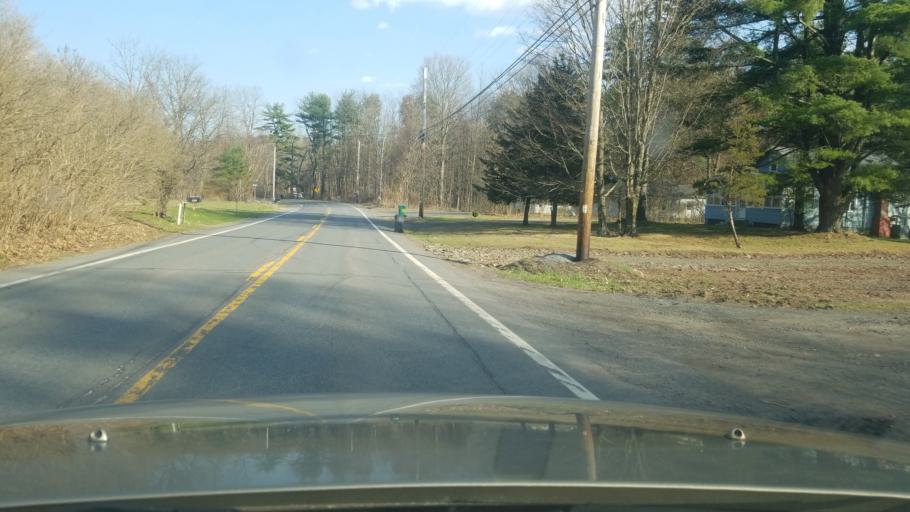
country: US
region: New York
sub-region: Greene County
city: Palenville
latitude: 42.1613
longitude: -74.0065
